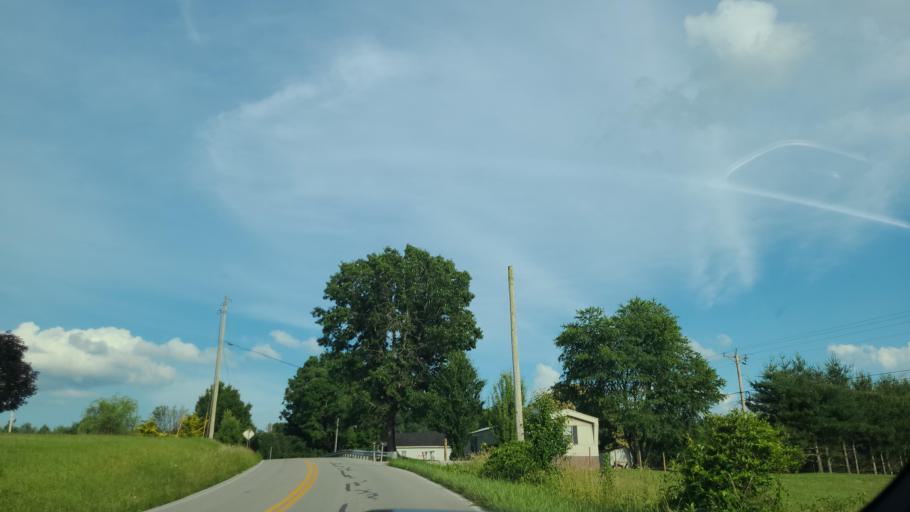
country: US
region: Kentucky
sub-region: Whitley County
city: Corbin
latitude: 36.9078
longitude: -84.2445
